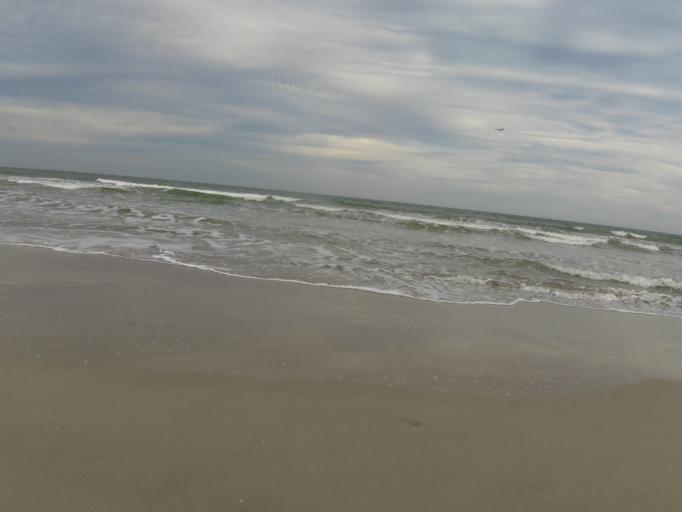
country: US
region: Florida
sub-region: Duval County
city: Neptune Beach
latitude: 30.3075
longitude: -81.3916
